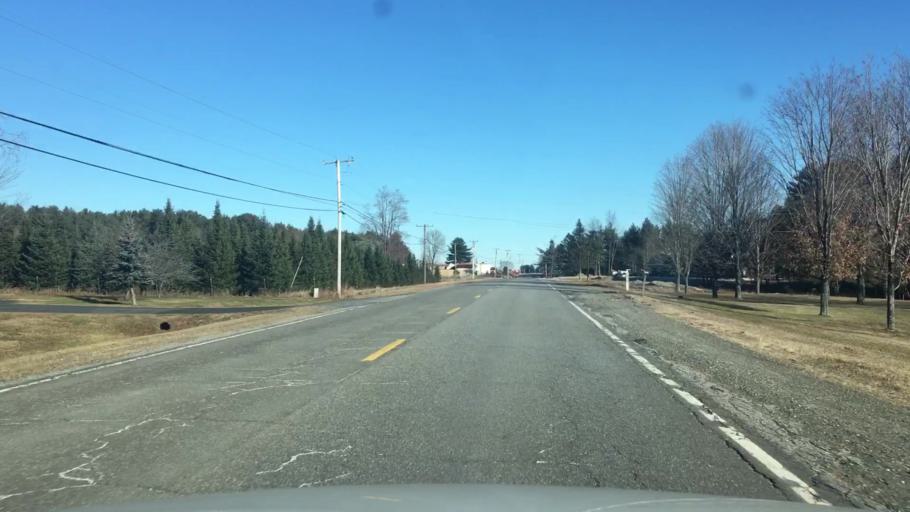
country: US
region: Maine
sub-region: Kennebec County
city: Winslow
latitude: 44.5526
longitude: -69.5879
